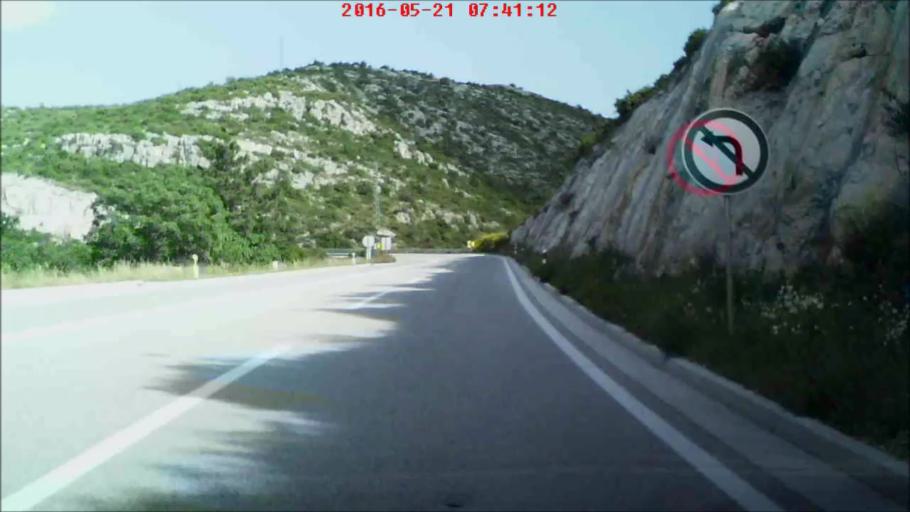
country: HR
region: Dubrovacko-Neretvanska
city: Podgora
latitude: 42.8060
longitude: 17.8180
